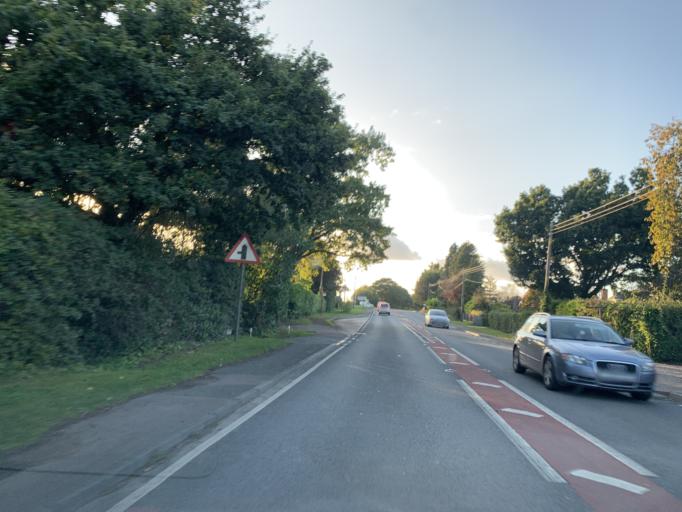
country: GB
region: England
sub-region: Hampshire
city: West Wellow
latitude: 50.9735
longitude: -1.6113
